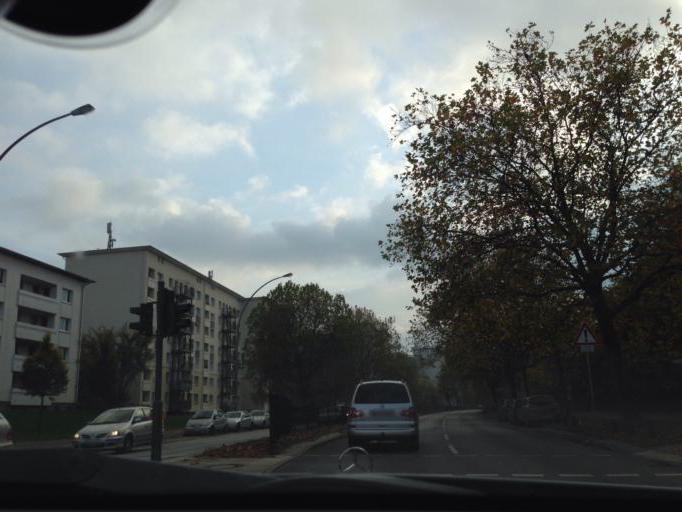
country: DE
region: Hamburg
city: Farmsen-Berne
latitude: 53.5787
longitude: 10.1281
